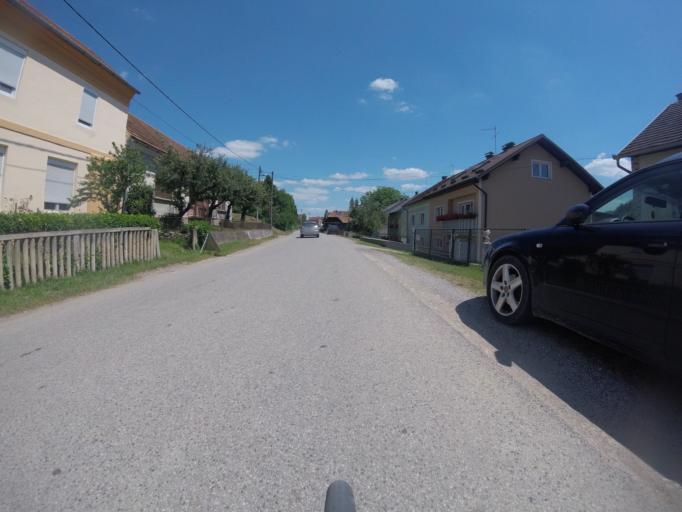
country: HR
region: Karlovacka
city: Ozalj
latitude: 45.6561
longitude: 15.5134
